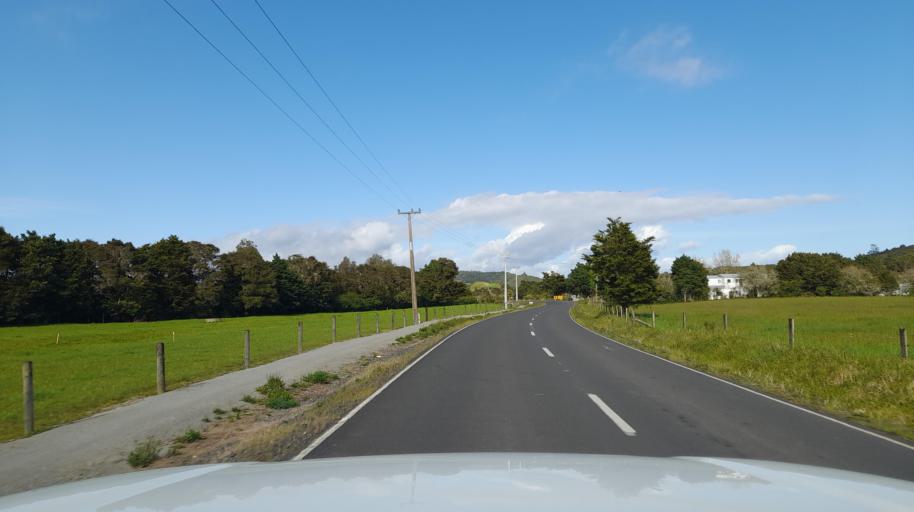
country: NZ
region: Northland
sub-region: Far North District
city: Moerewa
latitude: -35.4018
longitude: 173.9872
